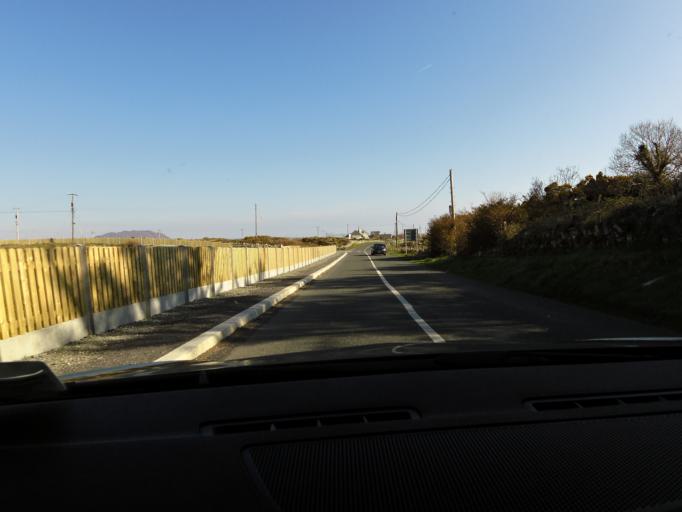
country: IE
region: Connaught
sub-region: County Galway
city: Clifden
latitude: 53.4302
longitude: -10.0745
